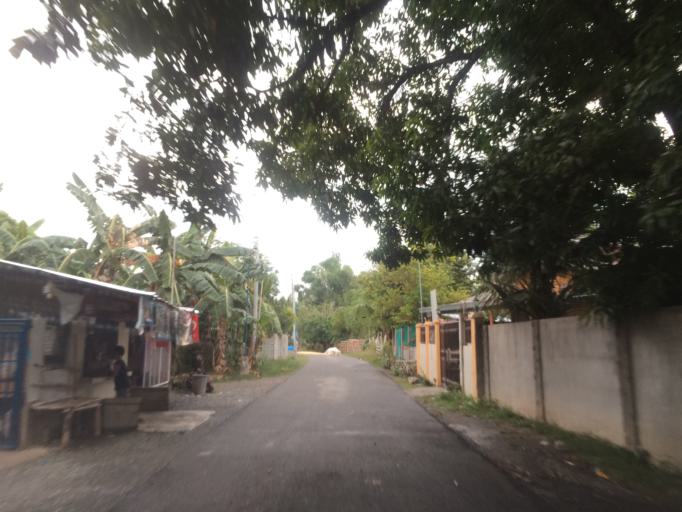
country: PH
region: Ilocos
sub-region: Province of Pangasinan
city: Anambongan
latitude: 15.8735
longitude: 120.3871
